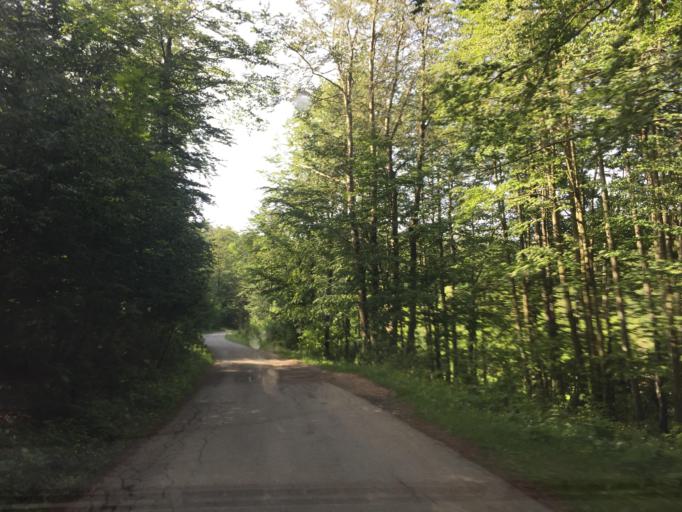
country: HR
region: Primorsko-Goranska
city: Podhum
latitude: 45.4367
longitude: 14.5630
